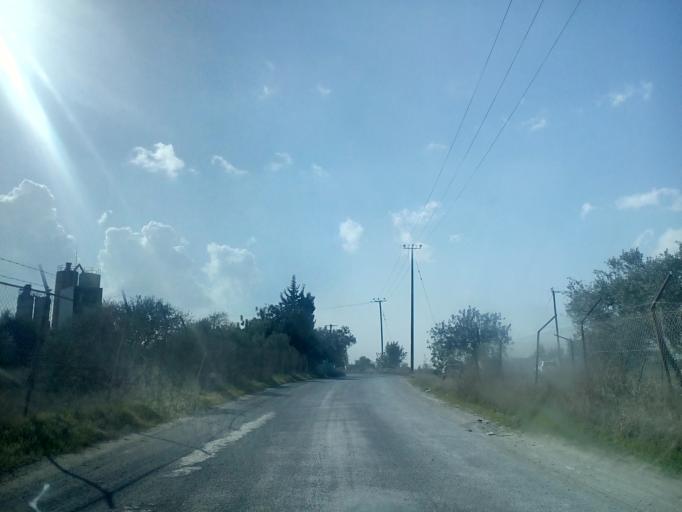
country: CY
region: Limassol
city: Ypsonas
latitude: 34.6766
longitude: 32.9757
